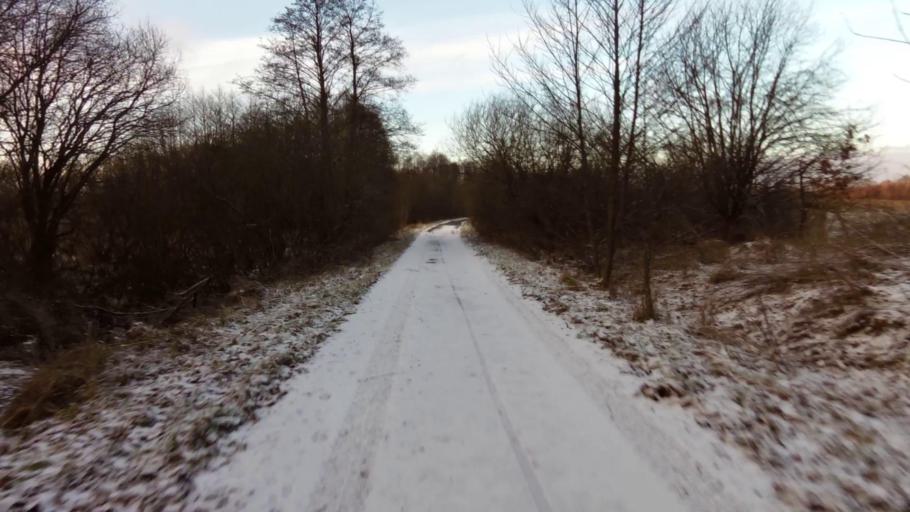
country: PL
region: West Pomeranian Voivodeship
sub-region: Powiat swidwinski
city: Polczyn-Zdroj
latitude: 53.6833
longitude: 16.0310
